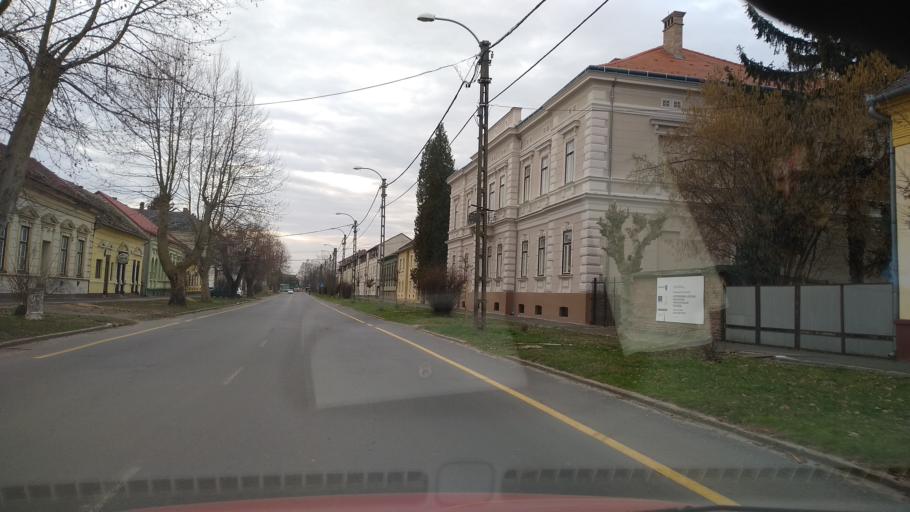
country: HU
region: Somogy
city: Barcs
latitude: 45.9555
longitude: 17.4490
